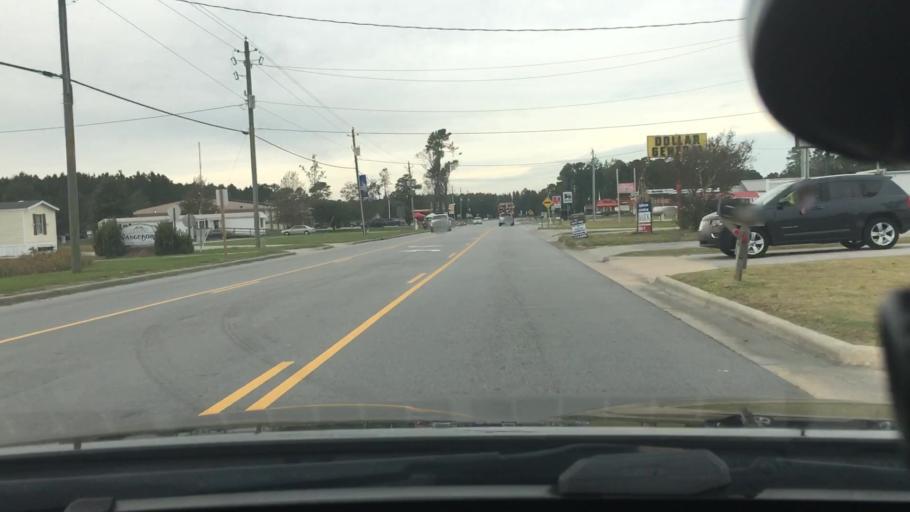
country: US
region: North Carolina
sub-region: Craven County
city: Vanceboro
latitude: 35.3092
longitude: -77.1586
